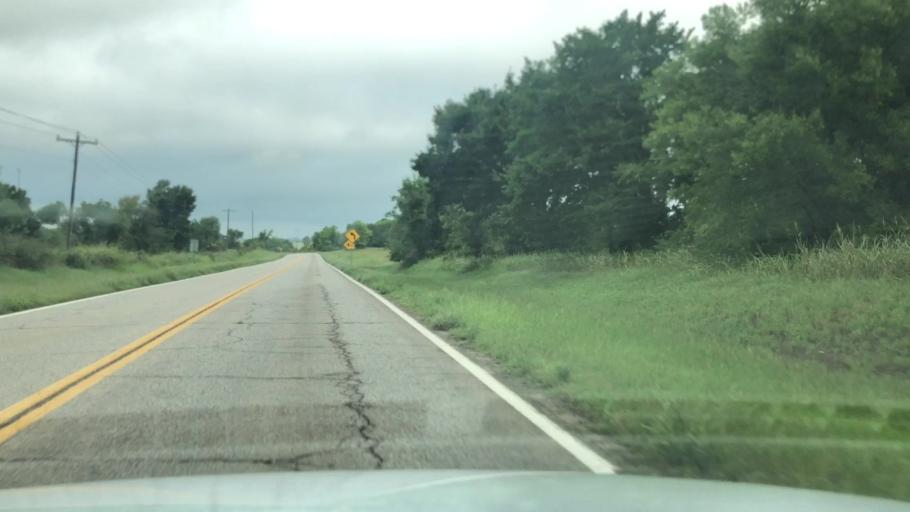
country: US
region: Oklahoma
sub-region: Nowata County
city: Nowata
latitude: 36.7114
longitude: -95.6605
